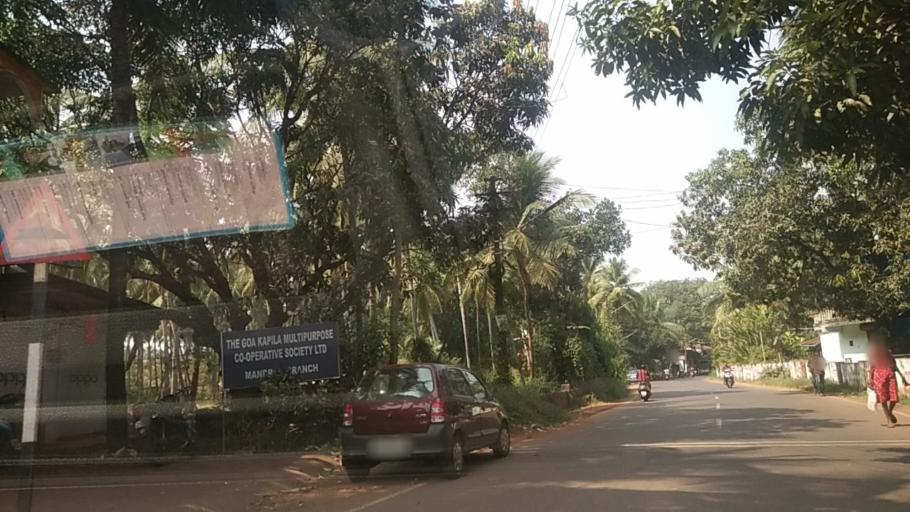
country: IN
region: Goa
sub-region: North Goa
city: Arambol
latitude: 15.6651
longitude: 73.7234
